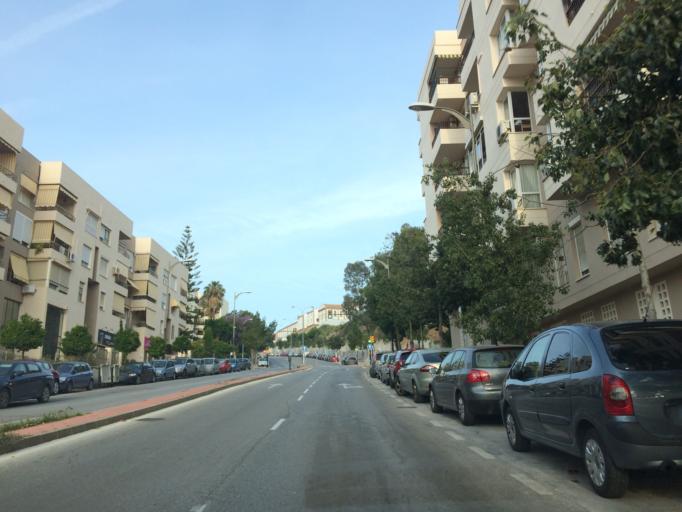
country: ES
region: Andalusia
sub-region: Provincia de Malaga
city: Malaga
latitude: 36.7349
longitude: -4.4138
